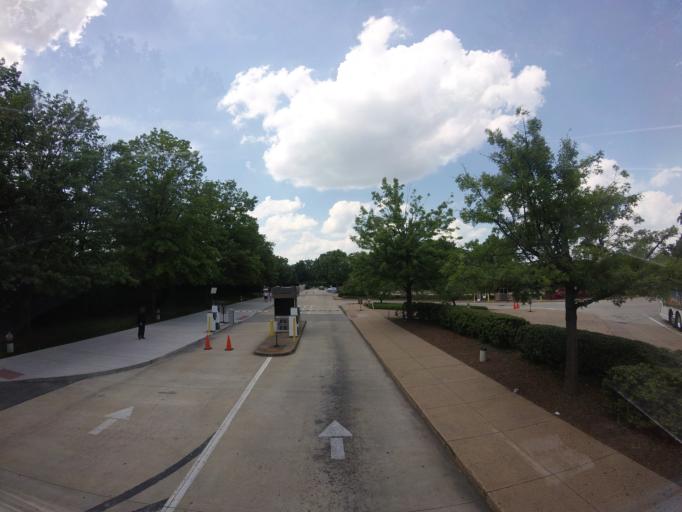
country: US
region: Washington, D.C.
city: Washington, D.C.
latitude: 38.8822
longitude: -77.0646
